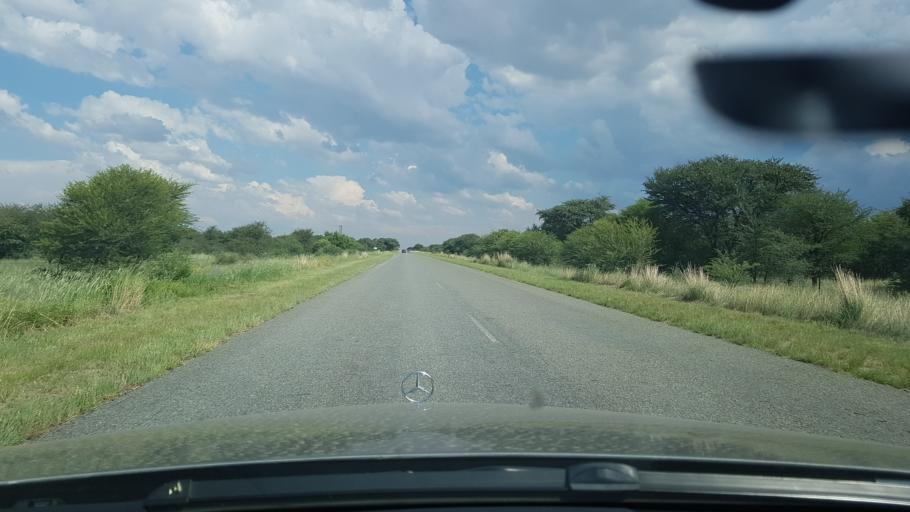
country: ZA
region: North-West
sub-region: Dr Ruth Segomotsi Mompati District Municipality
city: Bloemhof
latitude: -27.7928
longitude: 25.6156
